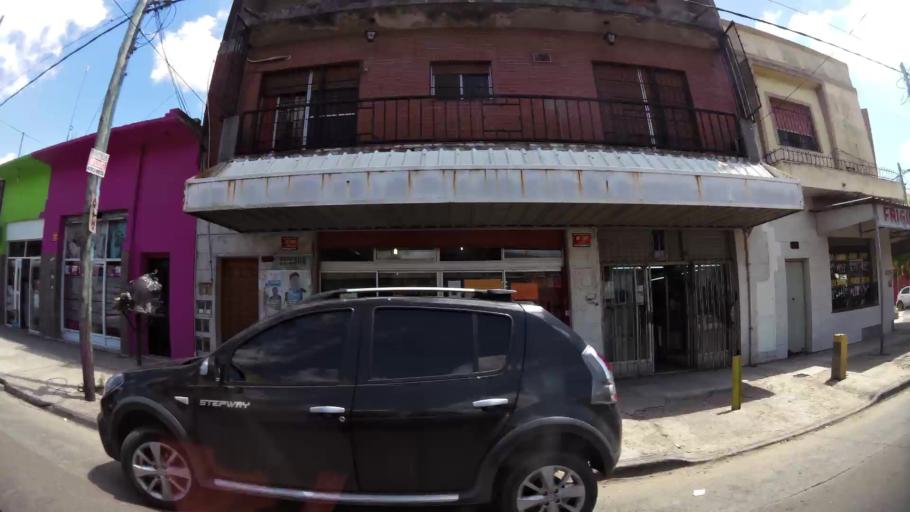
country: AR
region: Buenos Aires
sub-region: Partido de Lanus
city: Lanus
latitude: -34.6973
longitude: -58.4266
